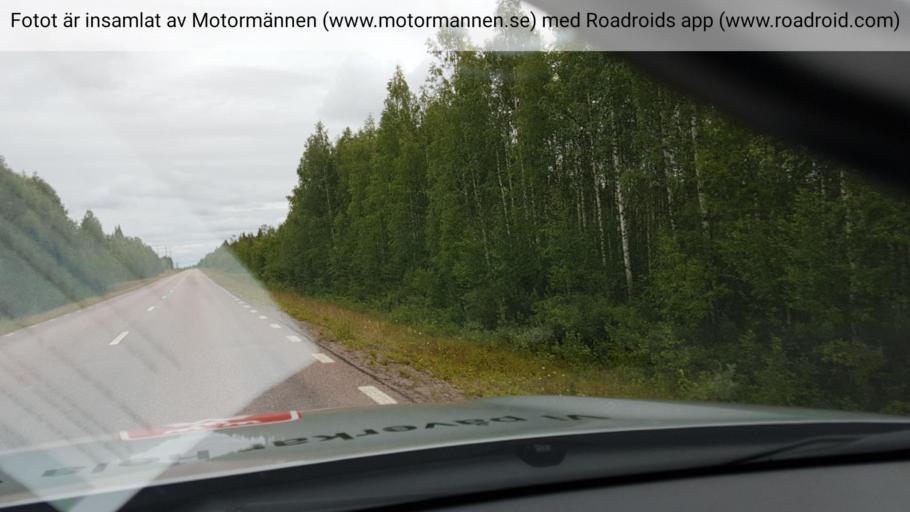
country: SE
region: Norrbotten
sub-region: Pajala Kommun
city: Pajala
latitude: 67.0903
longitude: 22.5632
